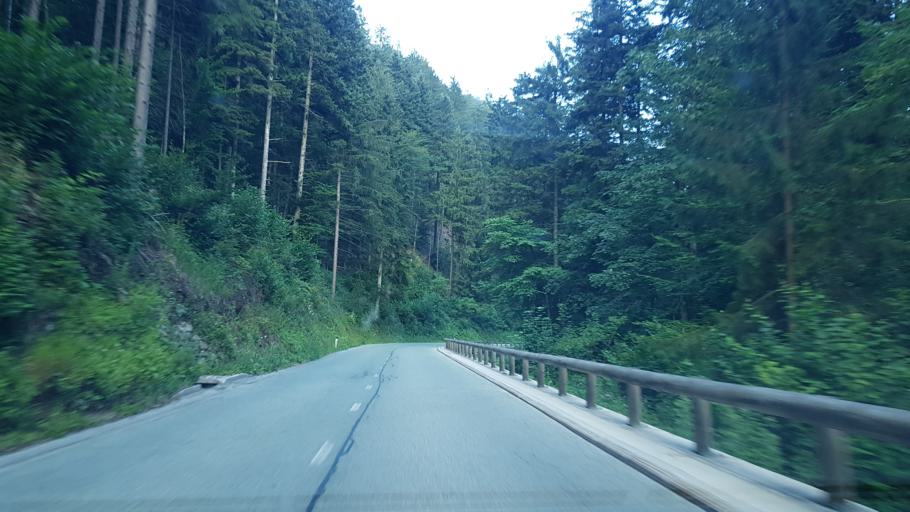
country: SI
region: Idrija
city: Spodnja Idrija
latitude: 46.0848
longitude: 14.0493
